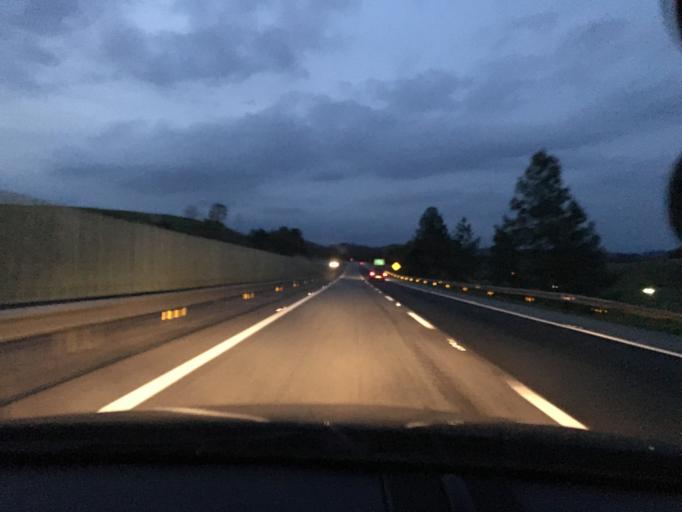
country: BR
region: Sao Paulo
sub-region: Santa Isabel
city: Santa Isabel
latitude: -23.3454
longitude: -46.1269
